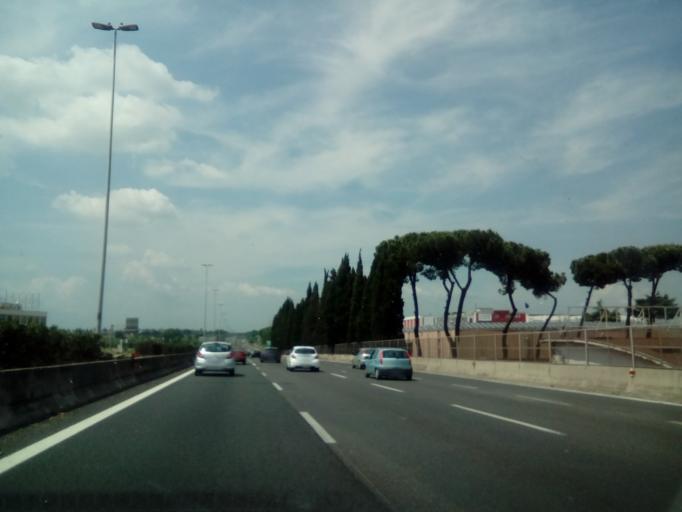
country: IT
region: Latium
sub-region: Citta metropolitana di Roma Capitale
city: Colle Verde
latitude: 41.9340
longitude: 12.6009
